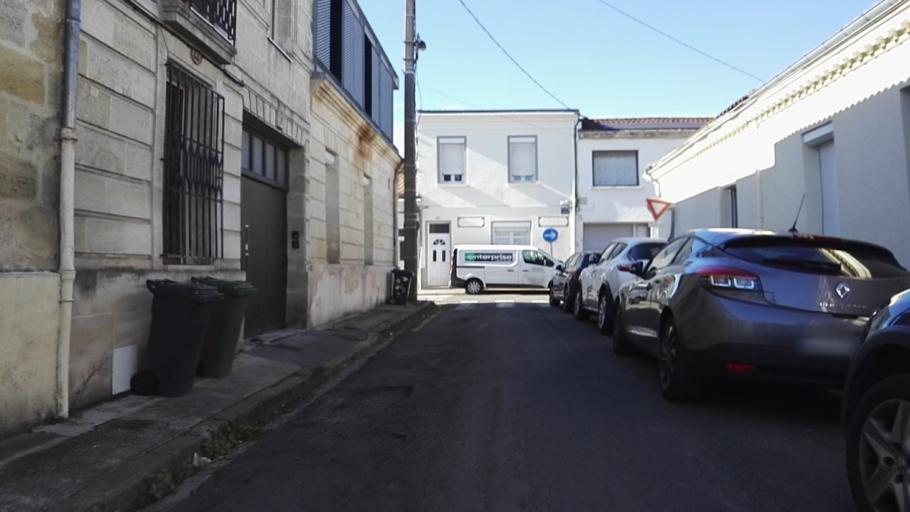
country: FR
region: Aquitaine
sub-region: Departement de la Gironde
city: Bordeaux
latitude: 44.8373
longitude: -0.6035
